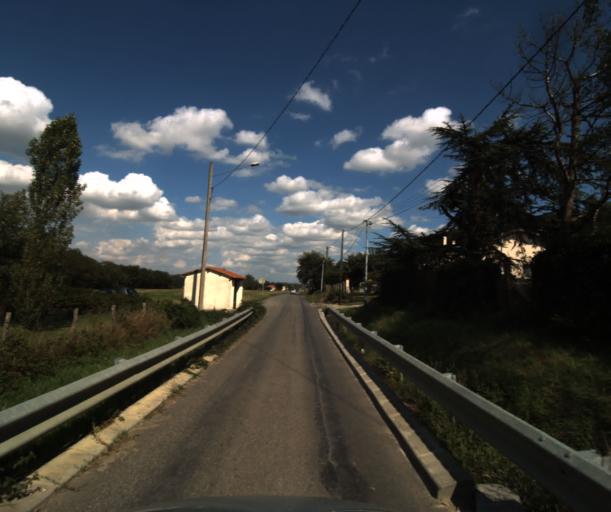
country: FR
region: Midi-Pyrenees
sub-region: Departement de la Haute-Garonne
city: Eaunes
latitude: 43.4160
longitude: 1.3611
